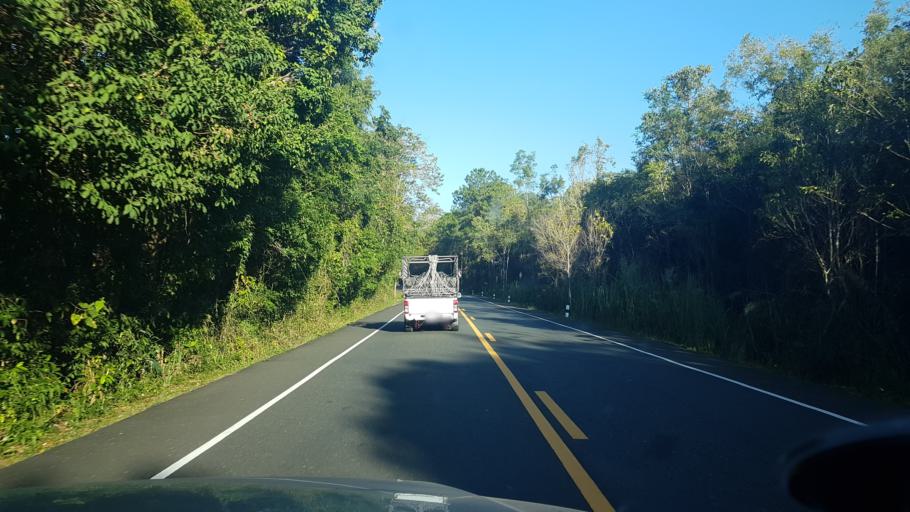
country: TH
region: Phetchabun
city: Nam Nao
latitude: 16.7052
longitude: 101.6062
